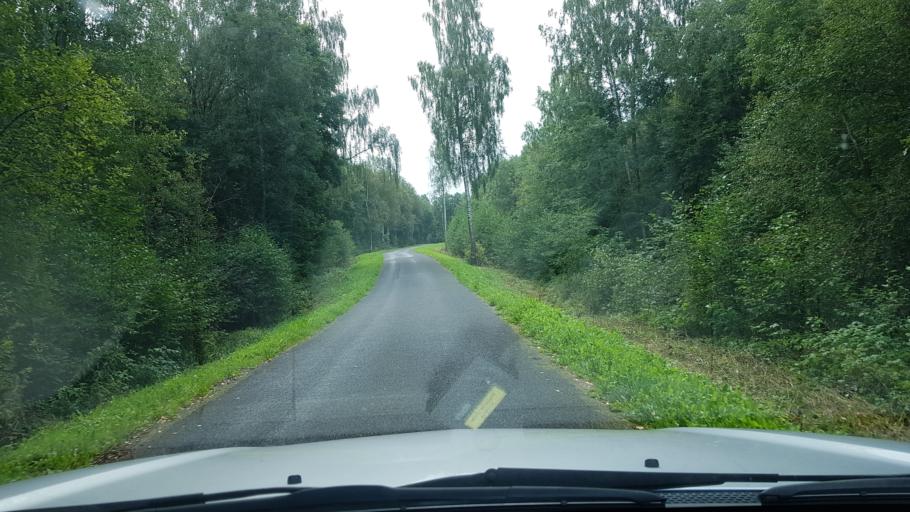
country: EE
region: Harju
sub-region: Rae vald
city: Jueri
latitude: 59.3572
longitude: 24.9361
